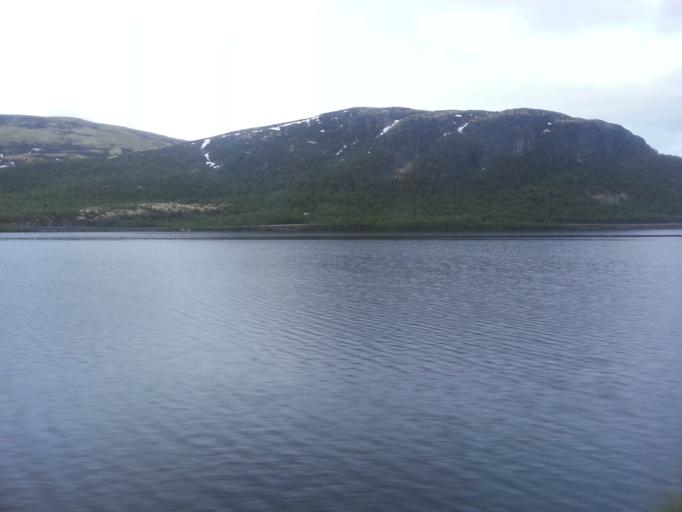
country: NO
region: Oppland
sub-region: Dovre
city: Dovre
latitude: 62.1775
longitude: 9.4065
